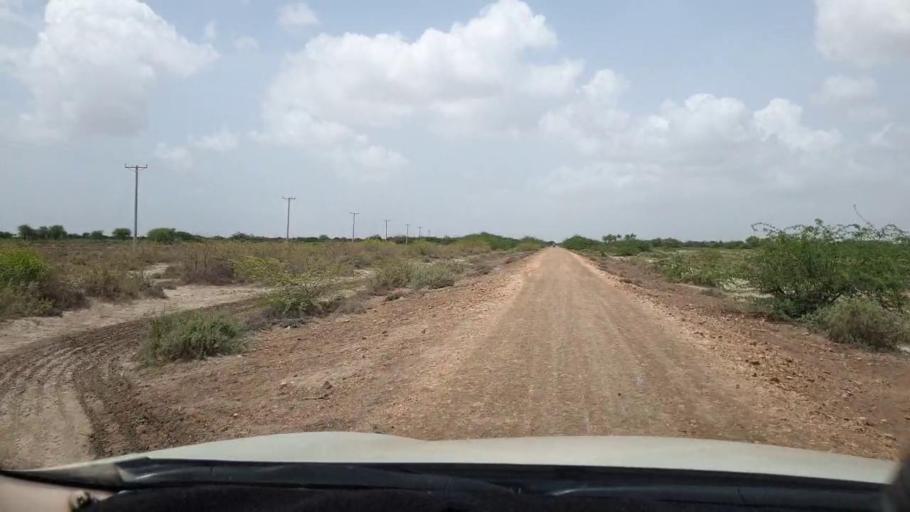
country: PK
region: Sindh
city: Kadhan
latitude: 24.3775
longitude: 68.8603
